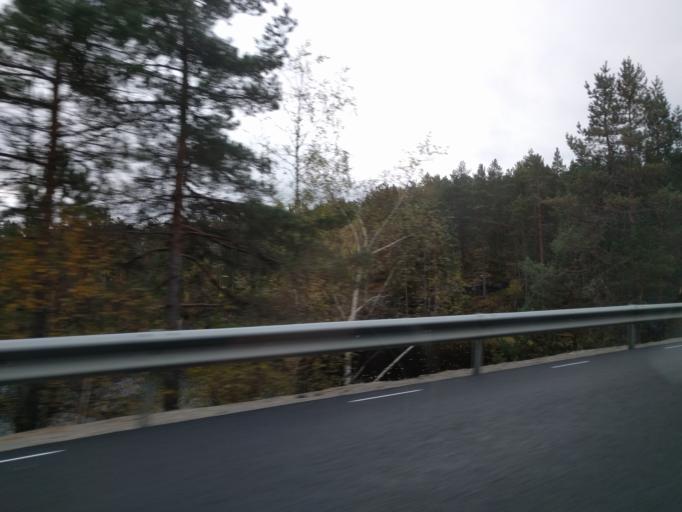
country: NO
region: Aust-Agder
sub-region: Iveland
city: Birketveit
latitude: 58.4579
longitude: 7.7921
